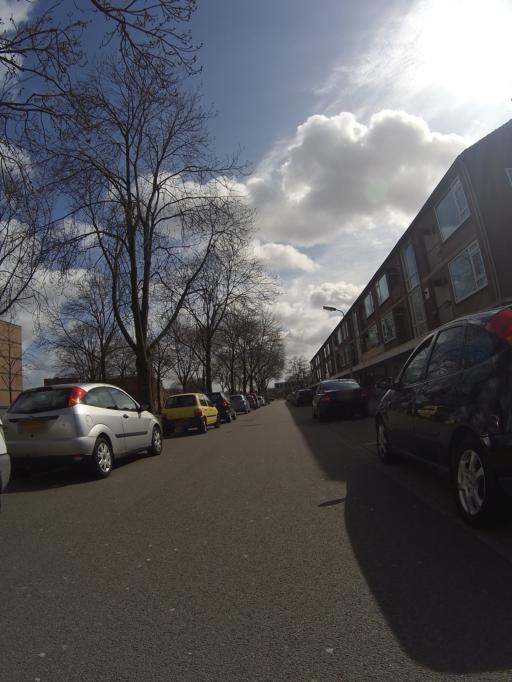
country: NL
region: Utrecht
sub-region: Gemeente Amersfoort
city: Amersfoort
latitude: 52.1649
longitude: 5.3858
